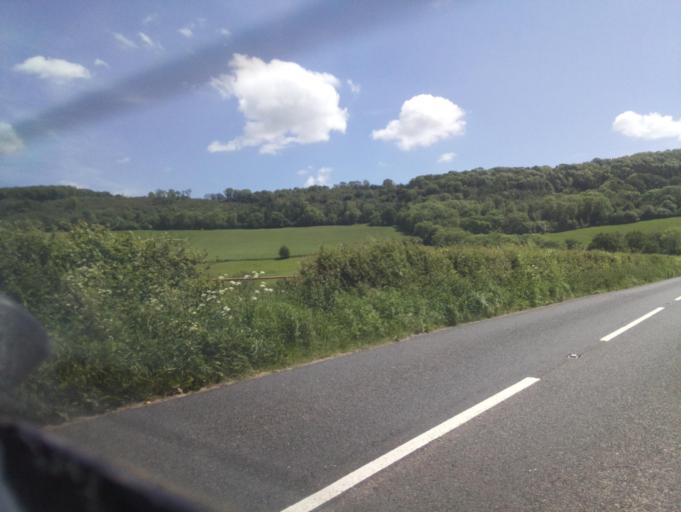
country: GB
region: Wales
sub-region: Monmouthshire
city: Monmouth
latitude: 51.7933
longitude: -2.7167
